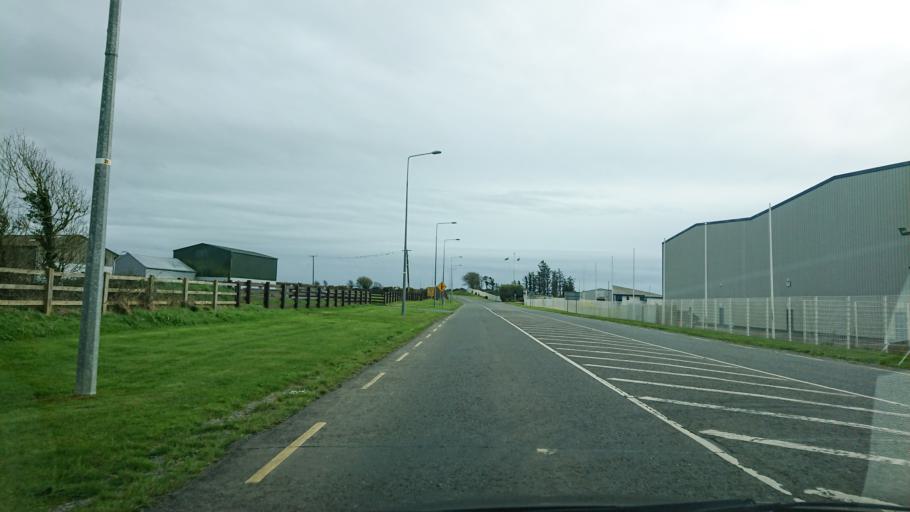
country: IE
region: Munster
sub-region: Waterford
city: Waterford
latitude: 52.1875
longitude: -7.0767
